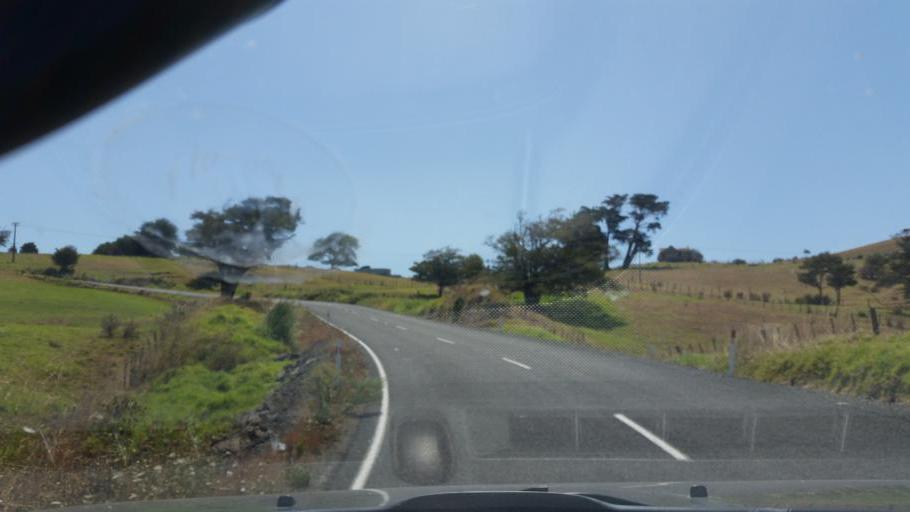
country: NZ
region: Northland
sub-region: Kaipara District
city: Dargaville
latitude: -36.0067
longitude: 173.9564
